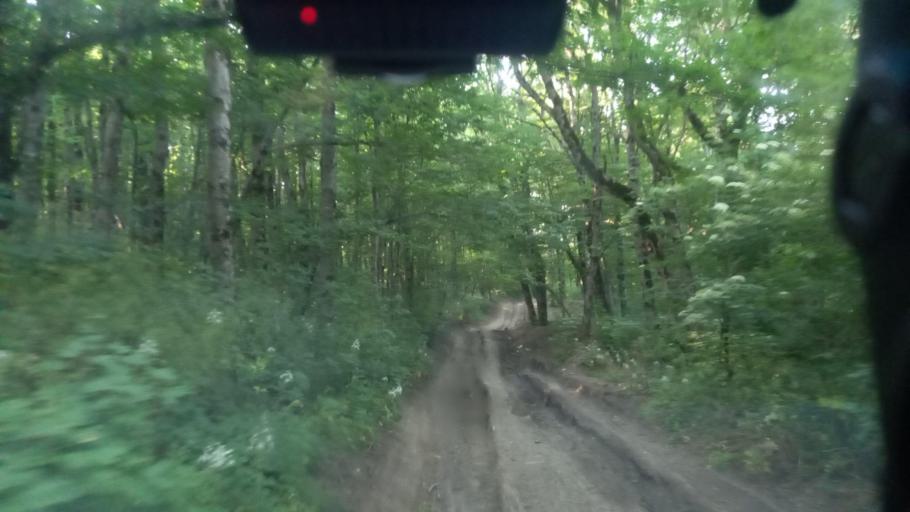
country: RU
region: Krasnodarskiy
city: Gelendzhik
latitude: 44.6198
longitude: 38.1883
